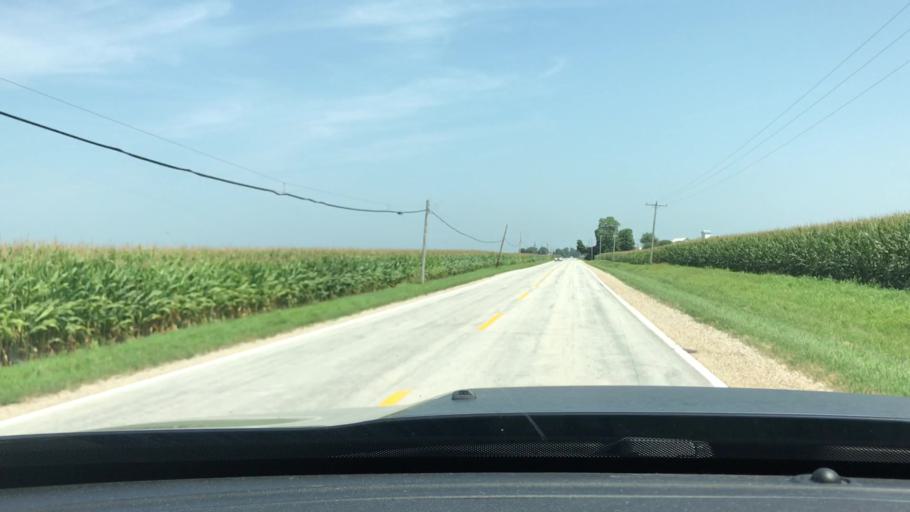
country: US
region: Illinois
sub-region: LaSalle County
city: Sheridan
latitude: 41.5005
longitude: -88.7326
